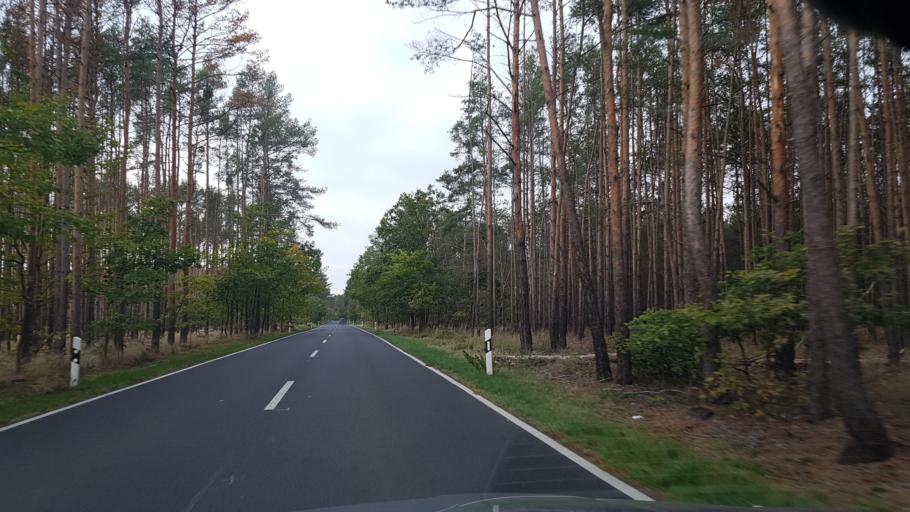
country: DE
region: Brandenburg
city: Bad Liebenwerda
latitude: 51.4845
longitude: 13.4545
